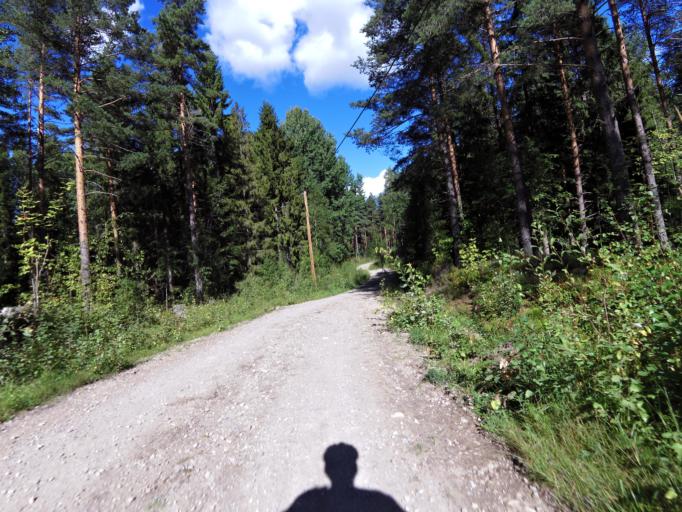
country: SE
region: Gaevleborg
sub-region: Gavle Kommun
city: Valbo
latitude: 60.7628
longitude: 16.9639
